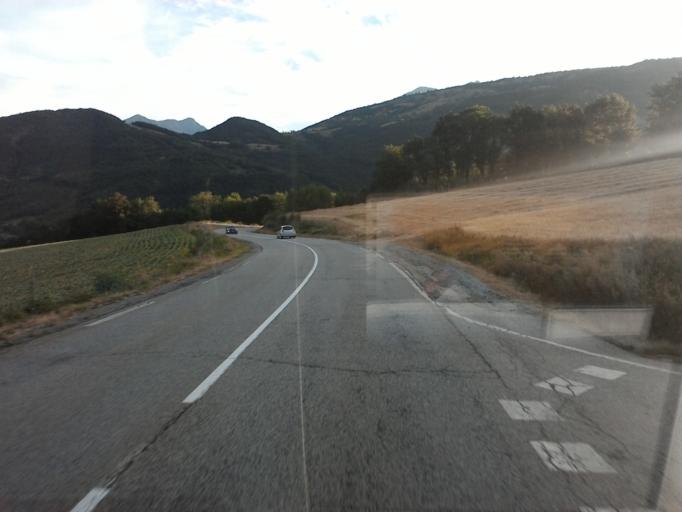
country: FR
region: Rhone-Alpes
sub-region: Departement de l'Isere
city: La Mure
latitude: 44.8561
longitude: 5.8569
